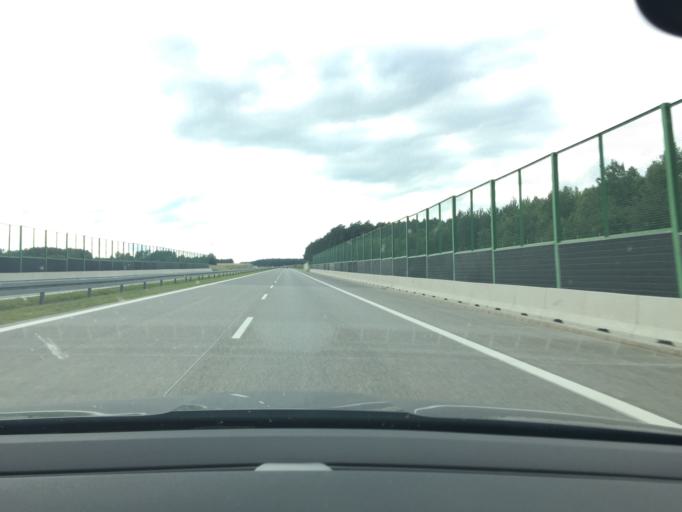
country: PL
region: Lubusz
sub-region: Powiat swiebodzinski
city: Lubrza
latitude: 52.3178
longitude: 15.4262
